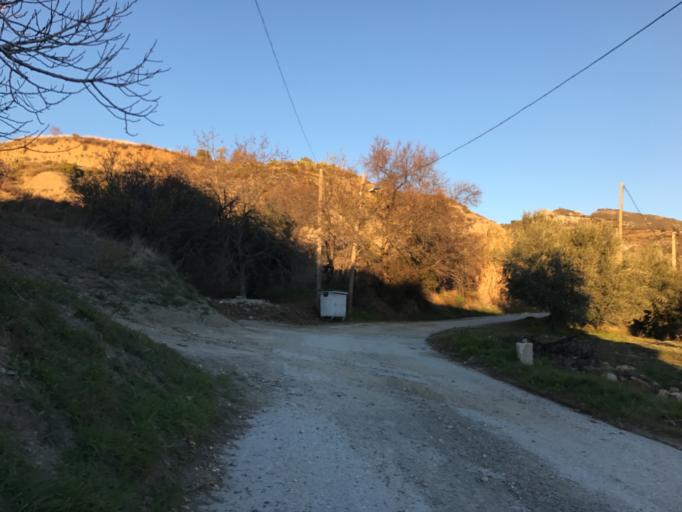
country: ES
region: Andalusia
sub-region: Provincia de Granada
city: Beas de Granada
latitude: 37.2221
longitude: -3.4749
